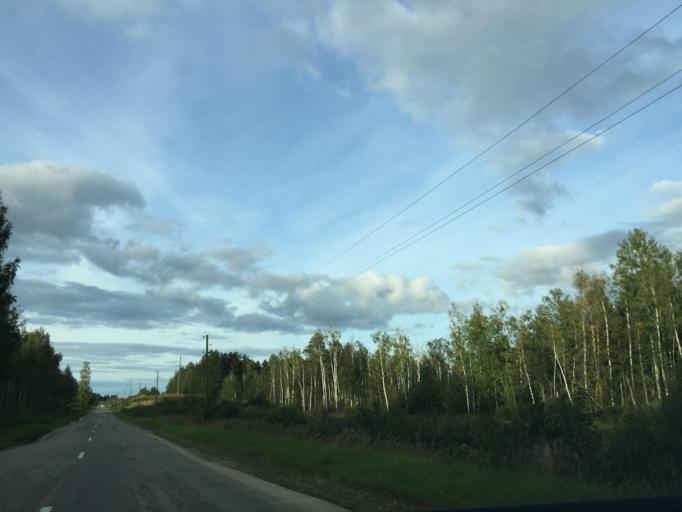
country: LV
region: Nereta
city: Nereta
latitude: 56.2337
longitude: 25.3251
